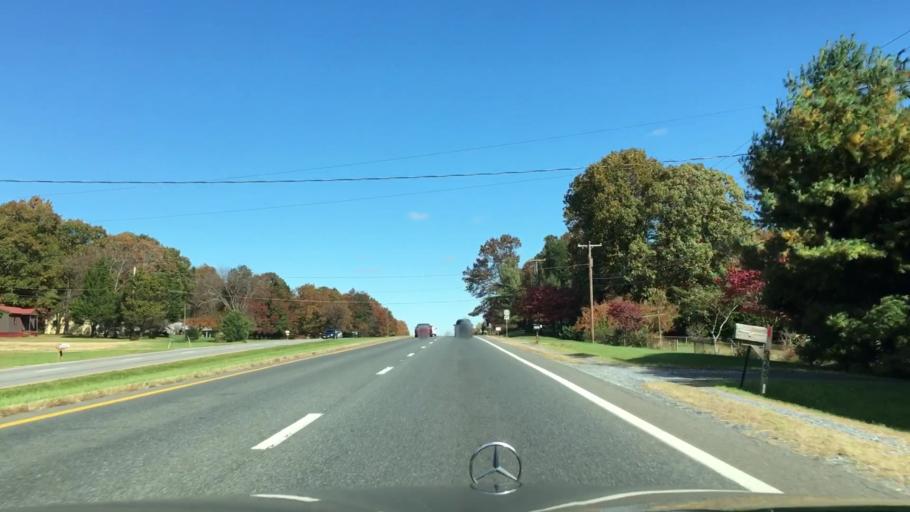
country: US
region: Virginia
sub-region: Campbell County
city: Rustburg
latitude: 37.2183
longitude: -79.1940
